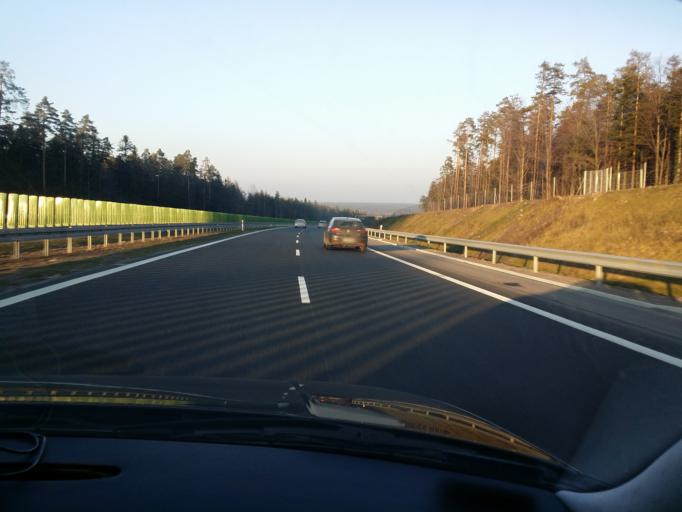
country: PL
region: Swietokrzyskie
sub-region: Powiat skarzyski
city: Skarzysko-Kamienna
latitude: 51.1442
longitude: 20.8344
